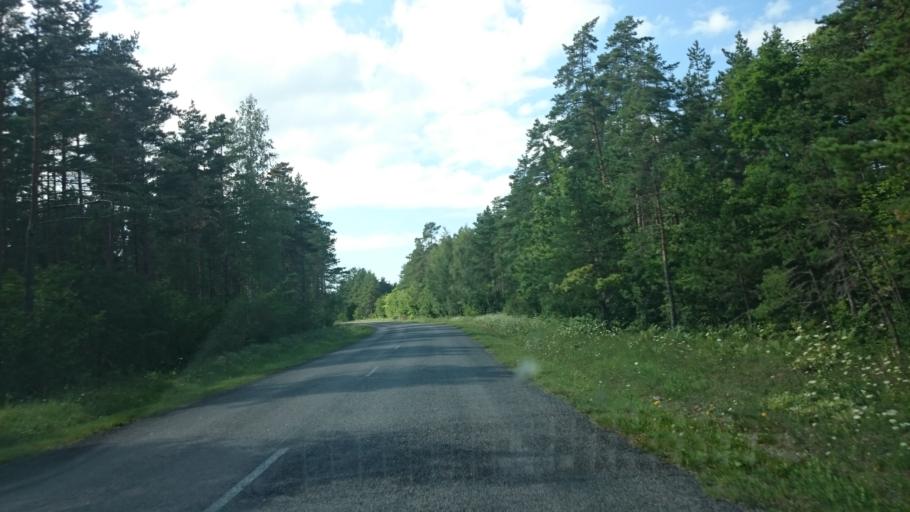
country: EE
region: Saare
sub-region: Orissaare vald
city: Orissaare
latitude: 58.5965
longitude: 22.9949
